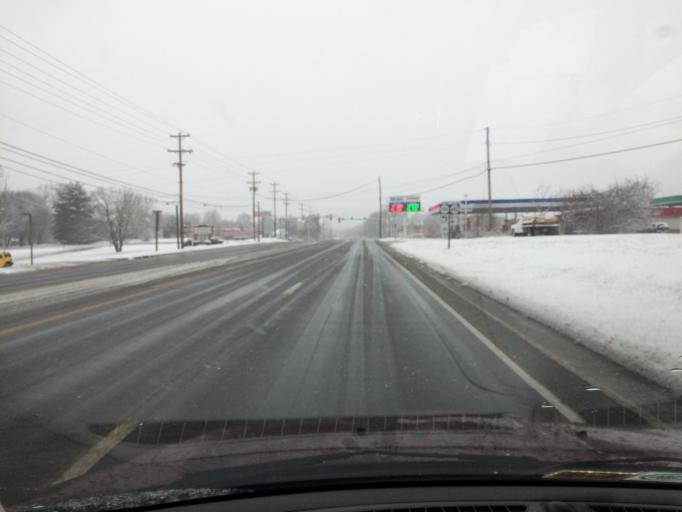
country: US
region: Virginia
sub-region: Amherst County
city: Madison Heights
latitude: 37.4597
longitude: -79.1196
